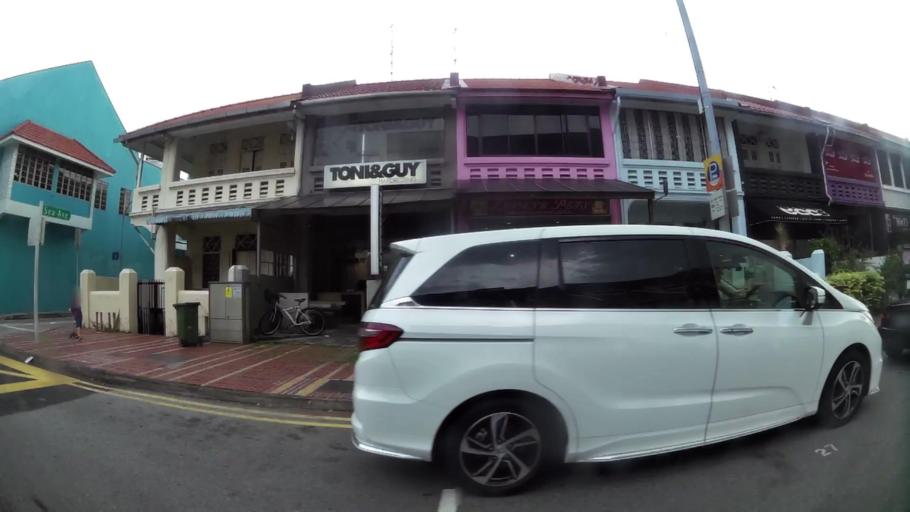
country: SG
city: Singapore
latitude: 1.3066
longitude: 103.9060
